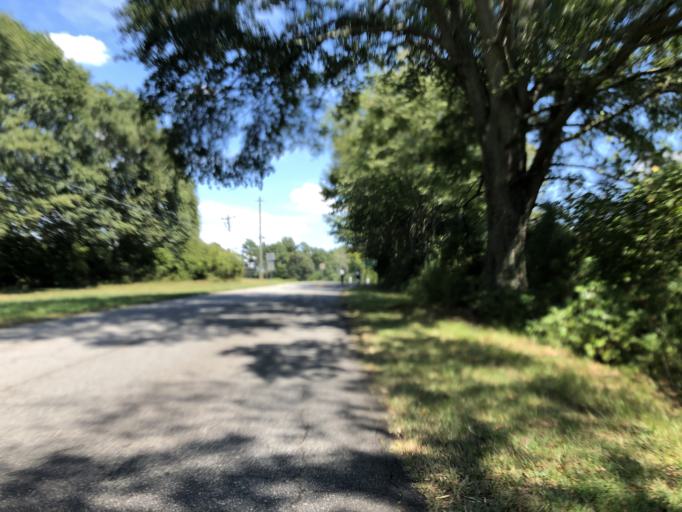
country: US
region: Georgia
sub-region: Fulton County
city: Palmetto
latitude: 33.5196
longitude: -84.6817
